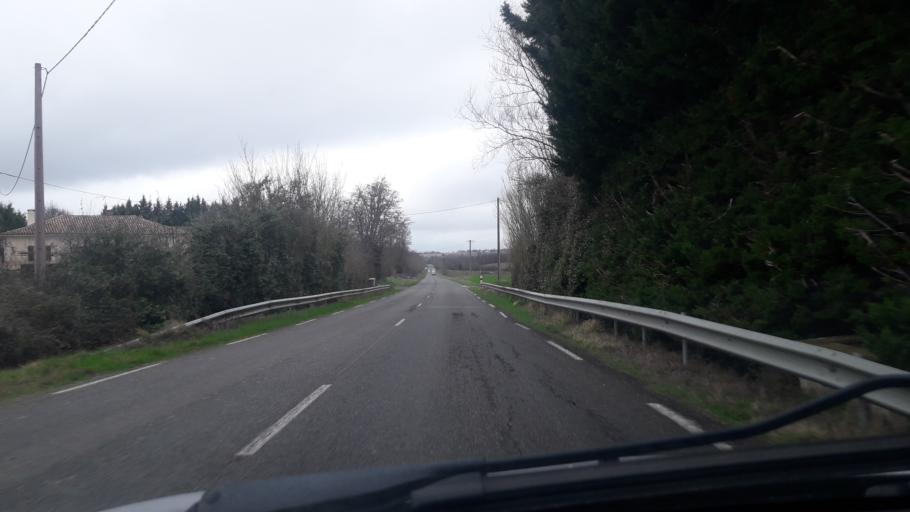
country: FR
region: Midi-Pyrenees
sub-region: Departement du Gers
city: Gimont
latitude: 43.6711
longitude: 1.0140
